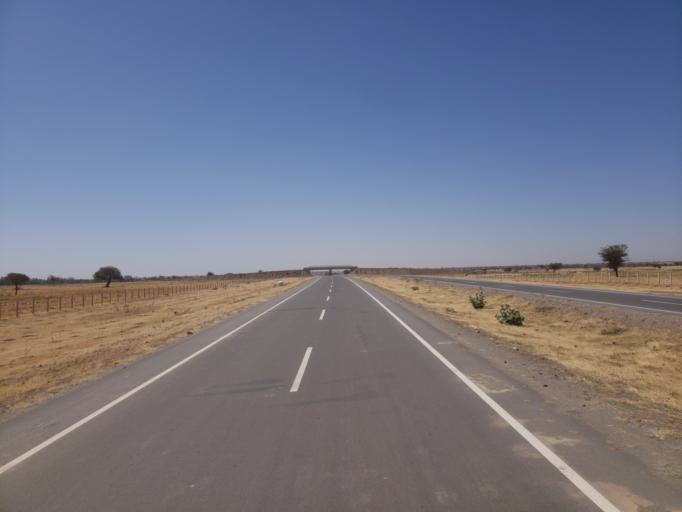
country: ET
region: Oromiya
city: Ziway
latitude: 8.2477
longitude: 38.8863
